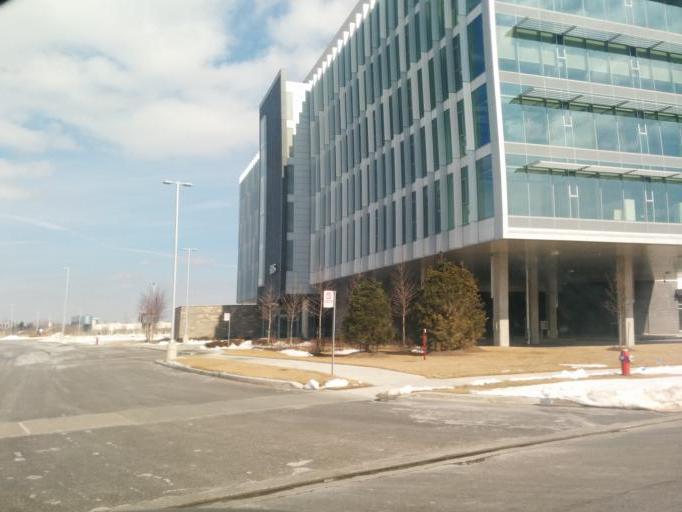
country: CA
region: Ontario
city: Etobicoke
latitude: 43.6495
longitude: -79.6079
